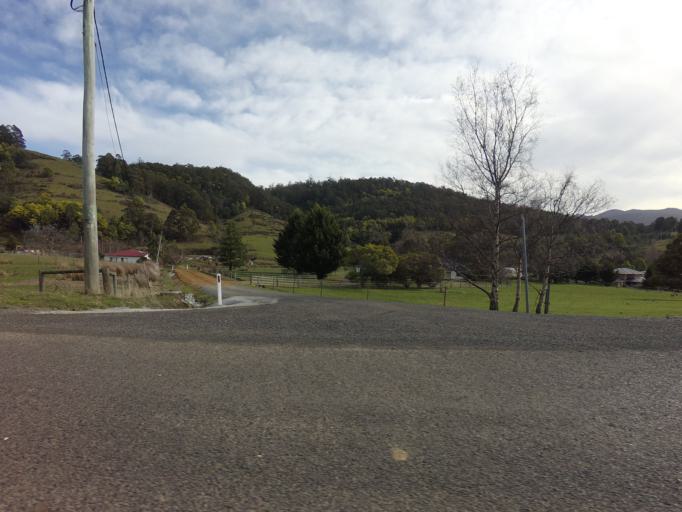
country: AU
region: Tasmania
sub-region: Kingborough
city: Margate
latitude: -42.9940
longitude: 147.1837
